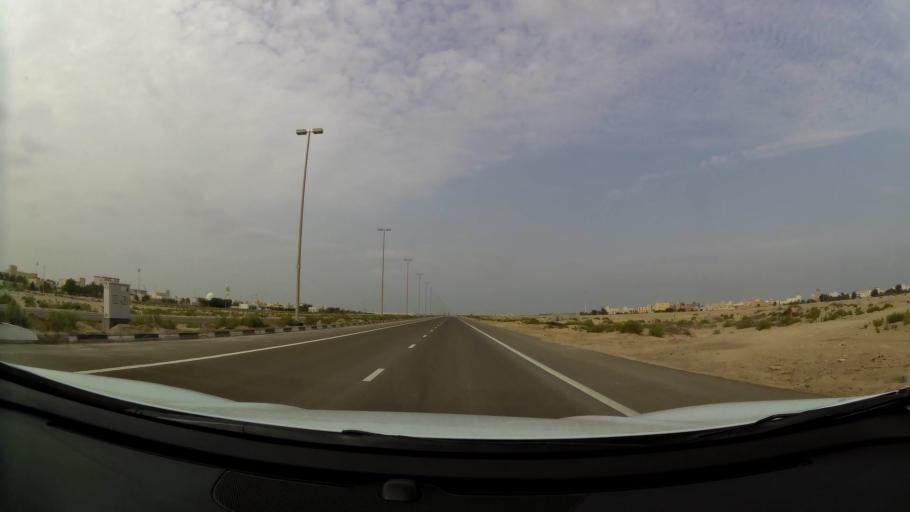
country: AE
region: Abu Dhabi
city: Abu Dhabi
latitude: 24.6380
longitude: 54.6748
